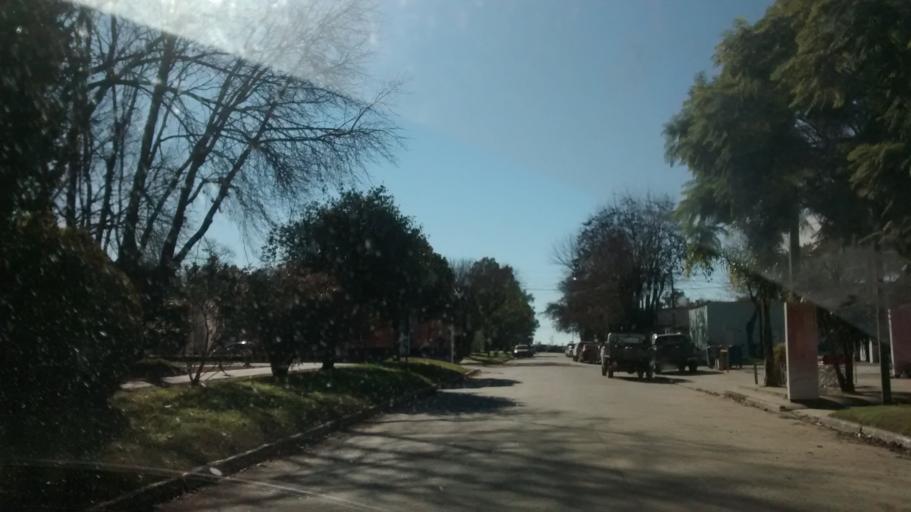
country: AR
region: Buenos Aires
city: Pila
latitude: -36.0045
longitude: -58.1404
